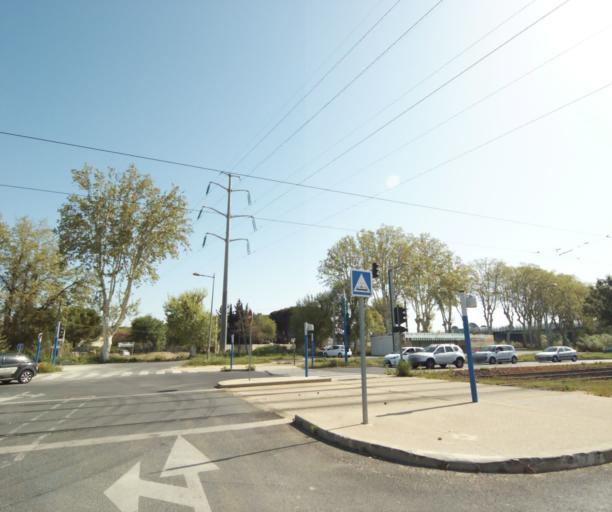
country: FR
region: Languedoc-Roussillon
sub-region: Departement de l'Herault
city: Lattes
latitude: 43.5910
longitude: 3.9086
